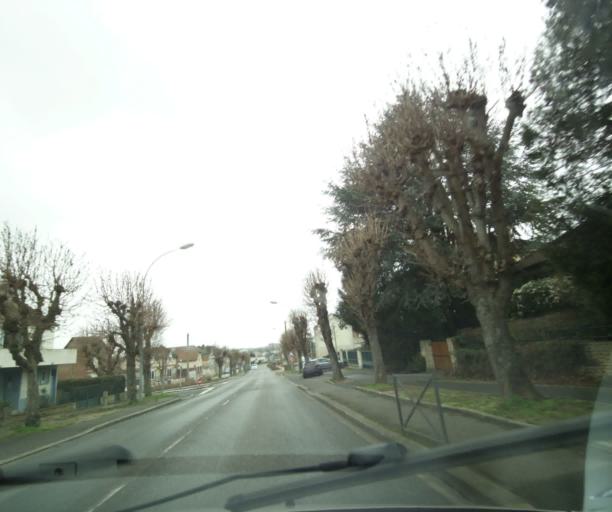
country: FR
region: Picardie
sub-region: Departement de l'Oise
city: Noyon
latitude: 49.5849
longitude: 2.9999
